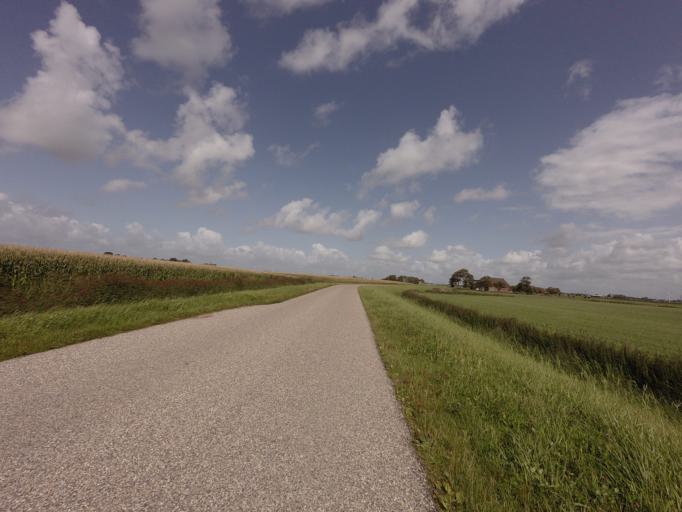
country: NL
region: Friesland
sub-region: Gemeente Harlingen
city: Harlingen
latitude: 53.1565
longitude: 5.4799
